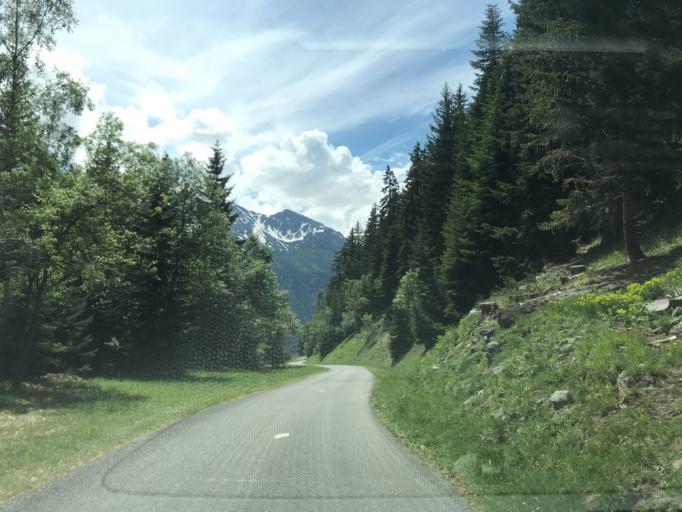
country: FR
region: Rhone-Alpes
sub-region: Departement de la Savoie
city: Modane
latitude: 45.2140
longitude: 6.6478
